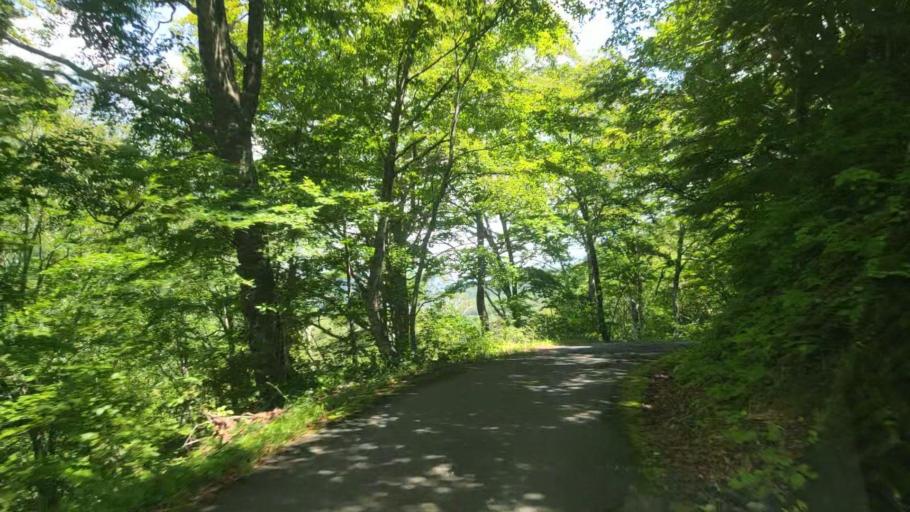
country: JP
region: Fukui
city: Ono
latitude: 35.7691
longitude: 136.5357
